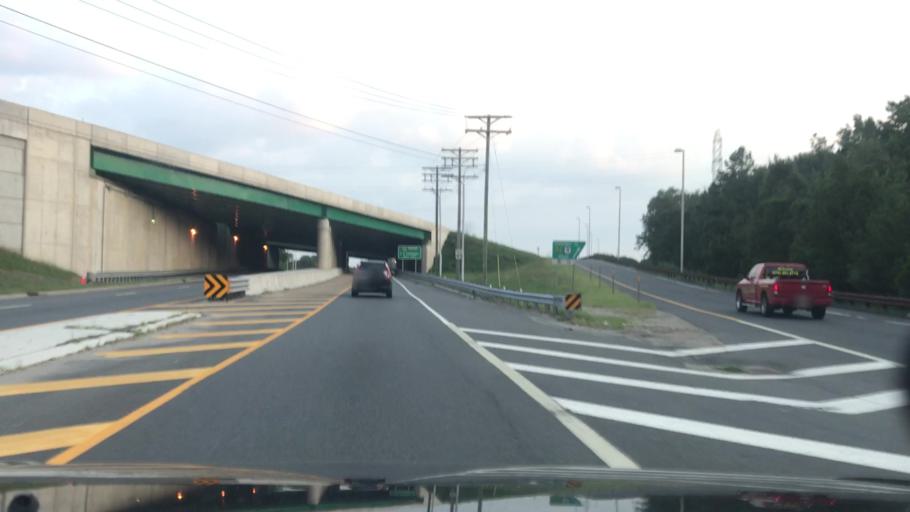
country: US
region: New Jersey
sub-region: Ocean County
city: Silver Ridge
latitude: 39.9897
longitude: -74.2110
